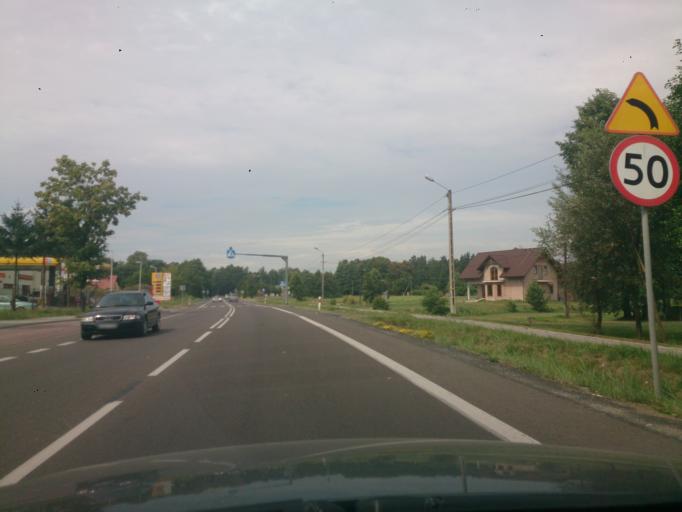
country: PL
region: Subcarpathian Voivodeship
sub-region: Powiat kolbuszowski
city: Dzikowiec
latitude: 50.2008
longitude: 21.8588
